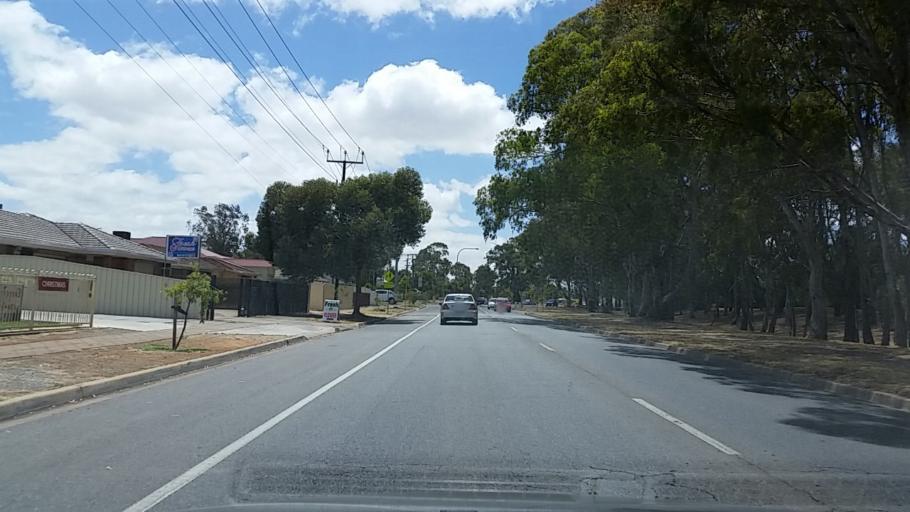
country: AU
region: South Australia
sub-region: Salisbury
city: Salisbury
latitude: -34.7698
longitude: 138.6189
